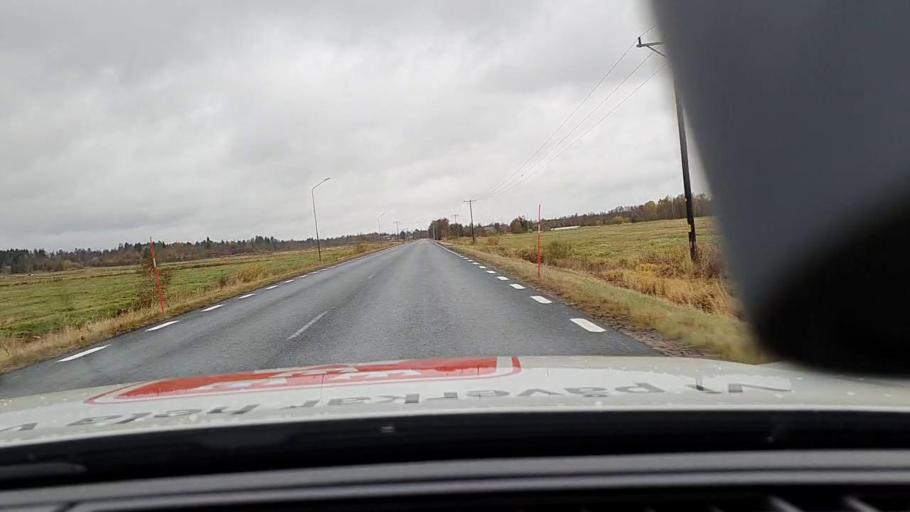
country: FI
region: Lapland
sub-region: Kemi-Tornio
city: Tornio
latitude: 65.9880
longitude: 24.0240
